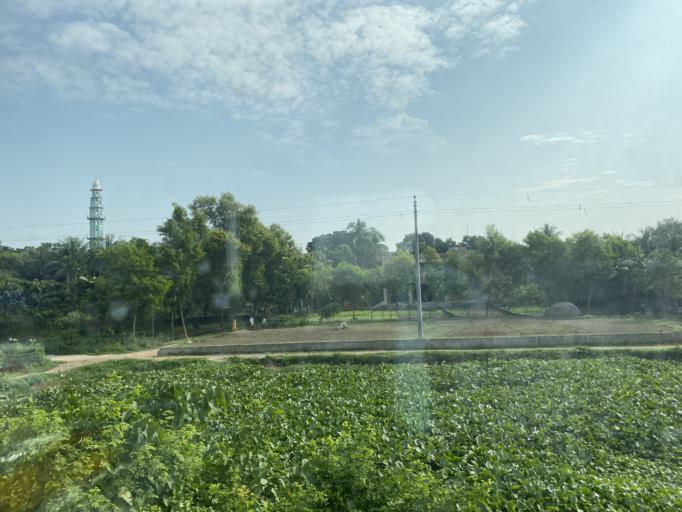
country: BD
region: Chittagong
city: Nabinagar
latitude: 23.9477
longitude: 91.1202
